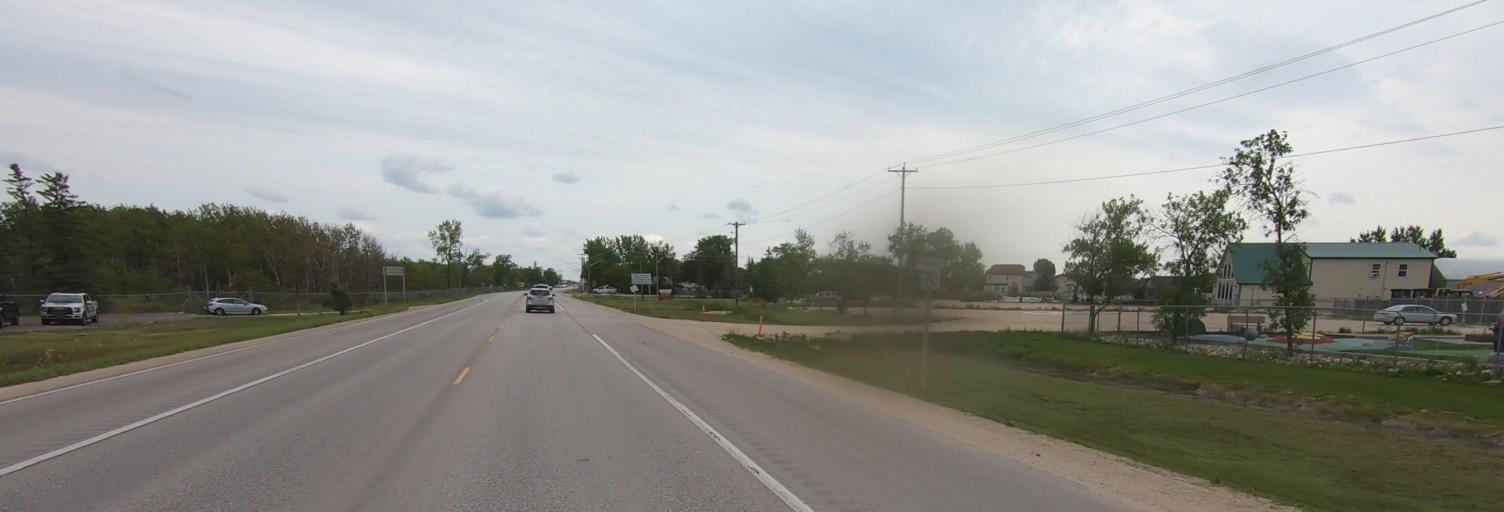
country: CA
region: Manitoba
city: Winnipeg
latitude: 49.8141
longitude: -97.2219
